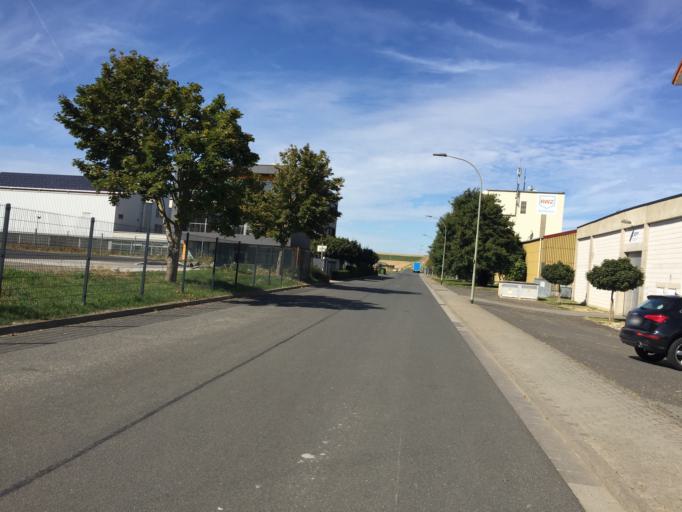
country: DE
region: Hesse
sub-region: Regierungsbezirk Giessen
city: Langgons
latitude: 50.4936
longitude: 8.6479
